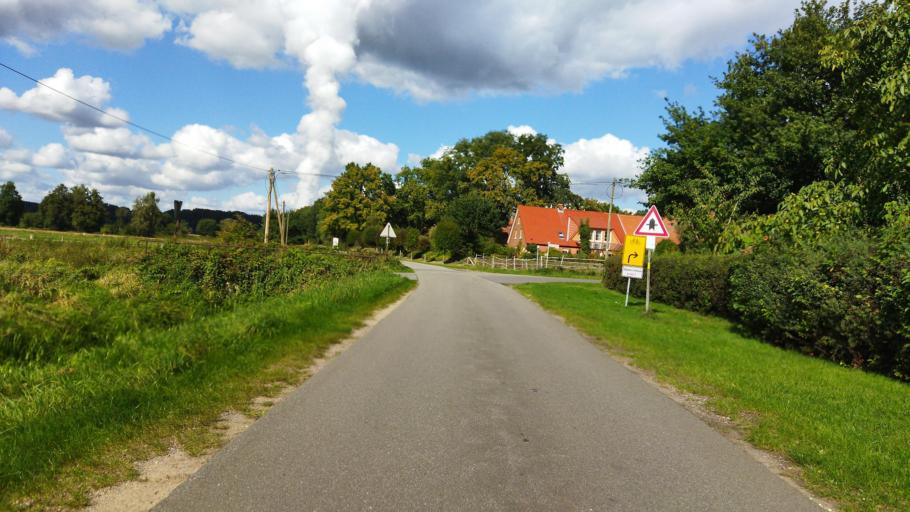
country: DE
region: Lower Saxony
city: Emsburen
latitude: 52.4461
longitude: 7.3376
